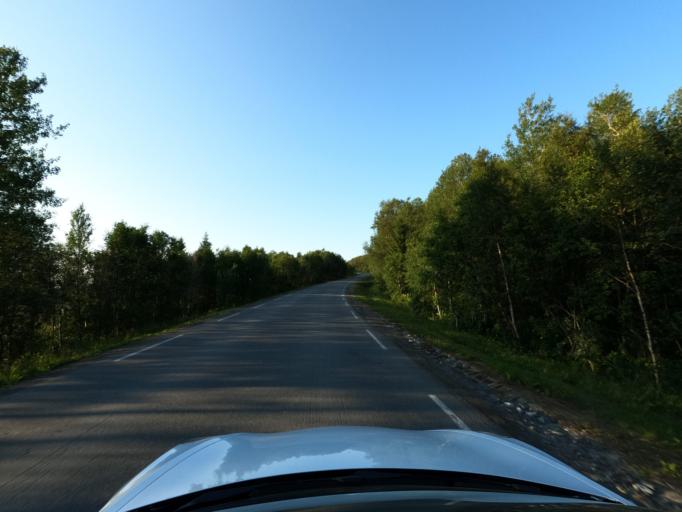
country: NO
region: Troms
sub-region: Skanland
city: Evenskjer
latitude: 68.4863
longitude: 16.7121
